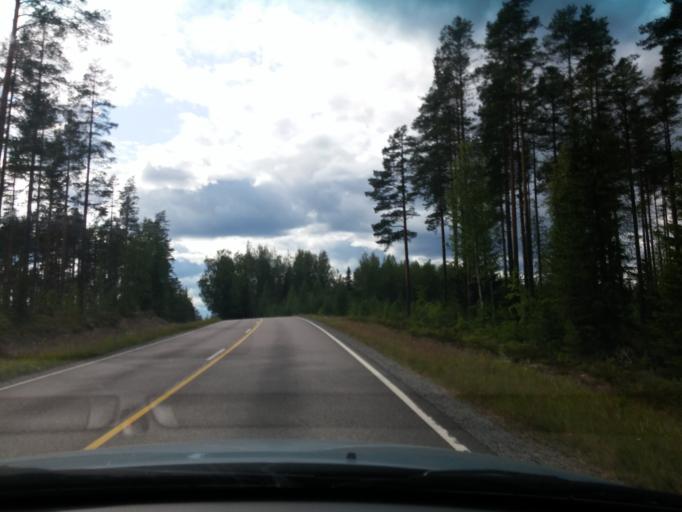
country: FI
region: Central Finland
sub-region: Saarijaervi-Viitasaari
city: Pylkoenmaeki
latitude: 62.6154
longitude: 24.7310
